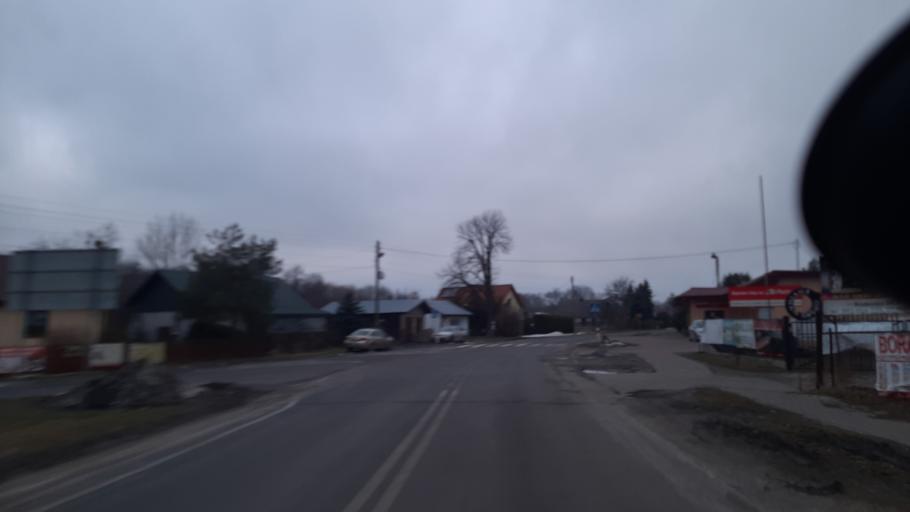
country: PL
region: Lublin Voivodeship
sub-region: Powiat parczewski
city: Sosnowica
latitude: 51.6080
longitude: 23.1254
